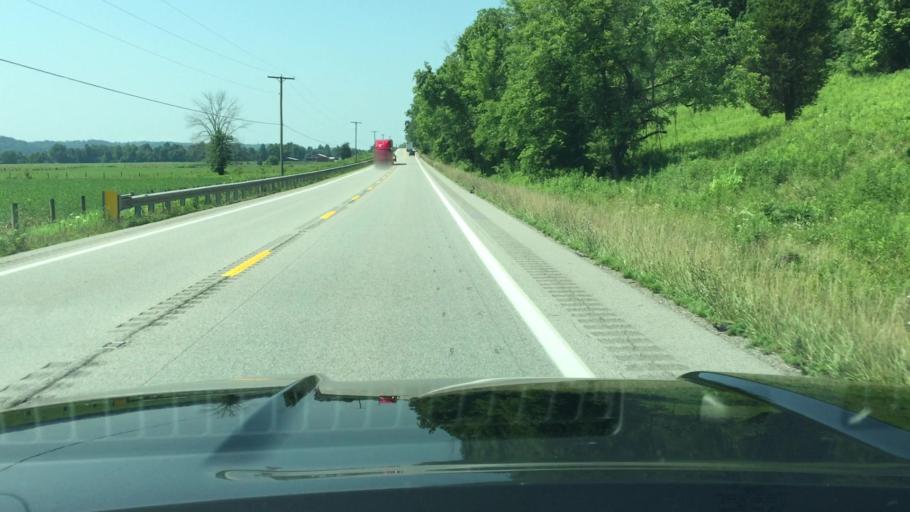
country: US
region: West Virginia
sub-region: Putnam County
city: Buffalo
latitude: 38.6485
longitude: -81.9717
